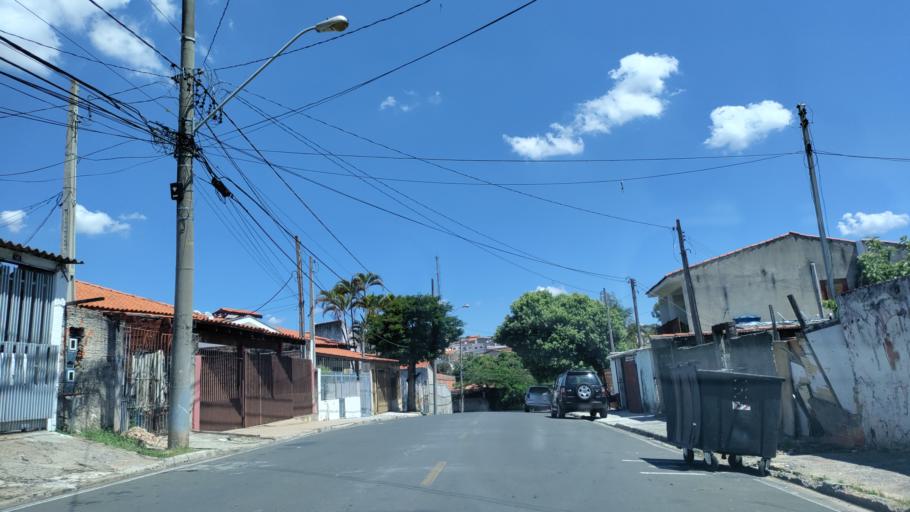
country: BR
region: Sao Paulo
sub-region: Sorocaba
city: Sorocaba
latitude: -23.4711
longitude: -47.4648
